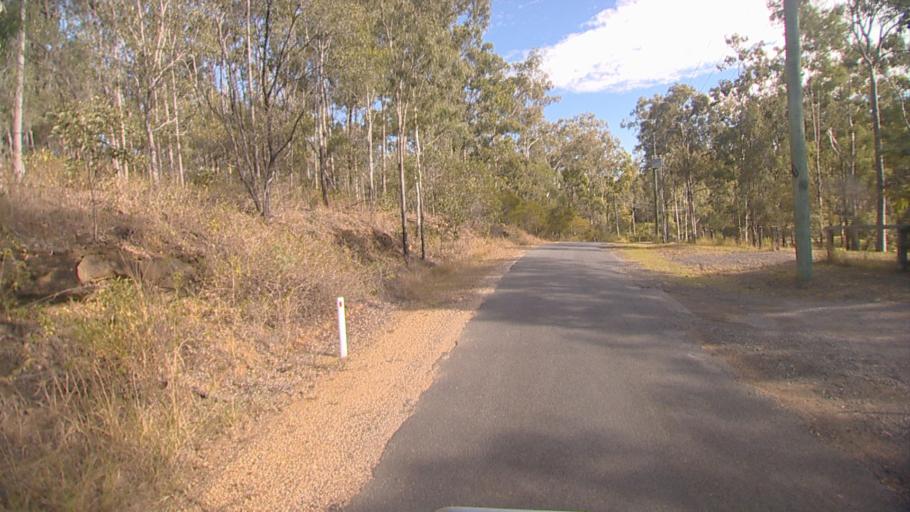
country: AU
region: Queensland
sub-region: Logan
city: Chambers Flat
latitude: -27.8251
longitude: 153.0792
